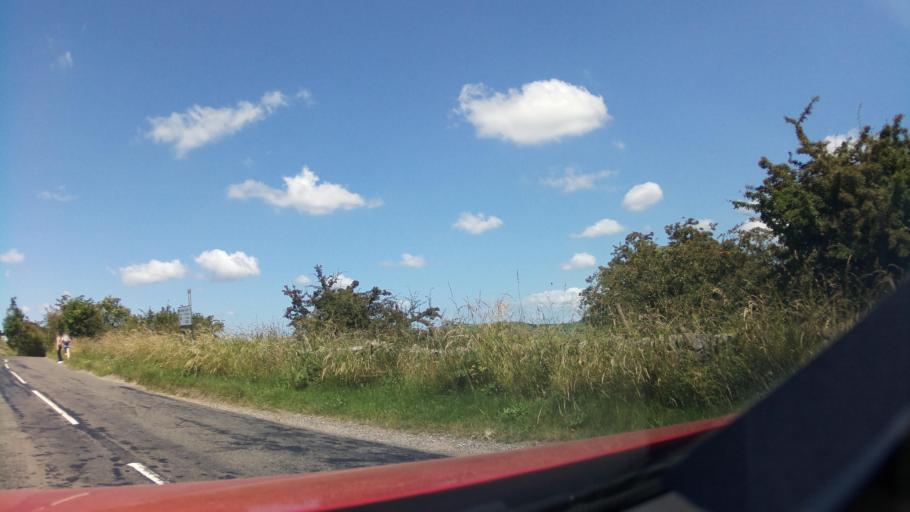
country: GB
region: England
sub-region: Derbyshire
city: Buxton
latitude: 53.1877
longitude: -1.8762
